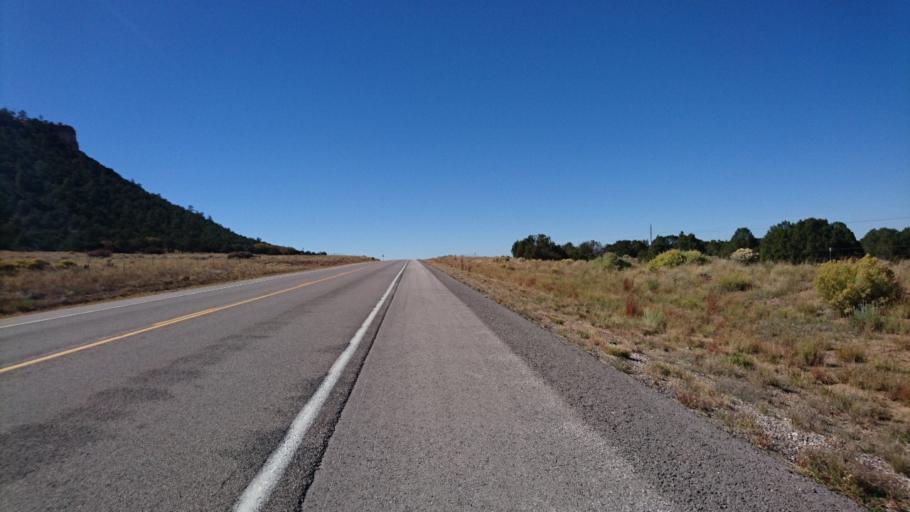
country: US
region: New Mexico
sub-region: McKinley County
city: Thoreau
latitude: 35.0449
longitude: -108.3075
